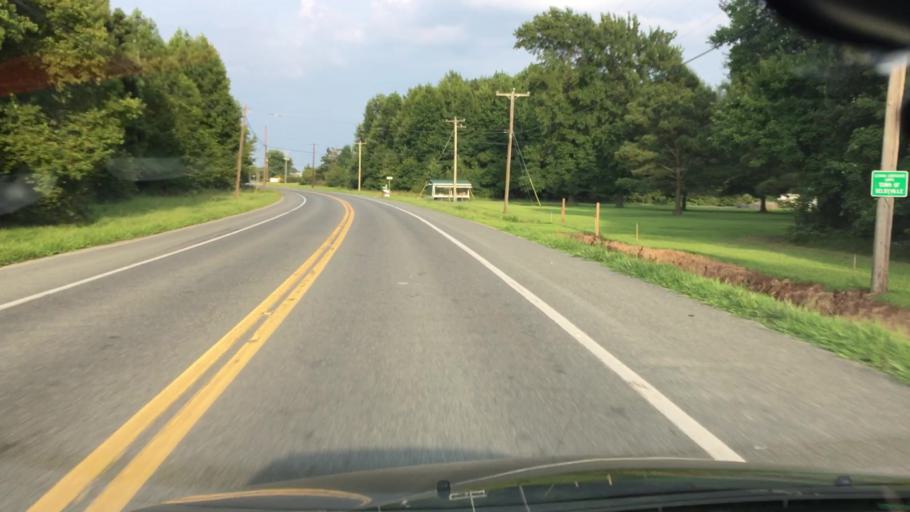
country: US
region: Delaware
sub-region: Sussex County
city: Selbyville
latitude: 38.4633
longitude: -75.1610
